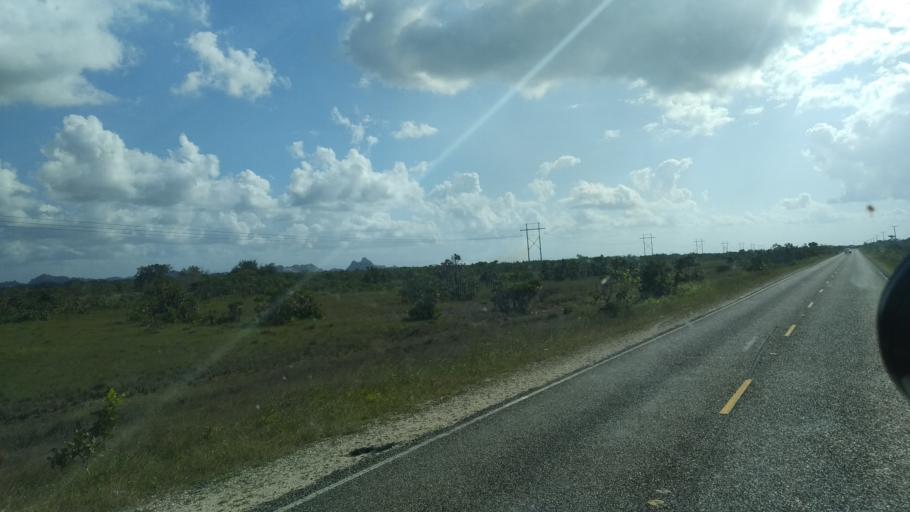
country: BZ
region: Belize
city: Belize City
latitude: 17.4332
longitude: -88.4246
